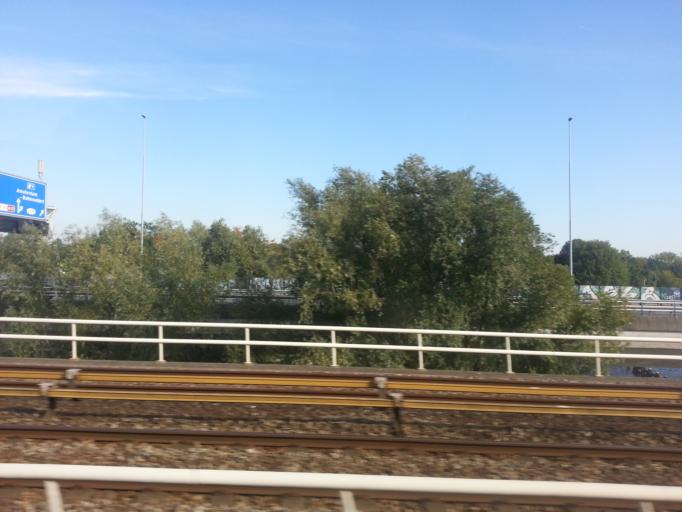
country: NL
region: North Holland
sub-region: Gemeente Ouder-Amstel
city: Ouderkerk aan de Amstel
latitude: 52.3332
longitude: 4.8984
